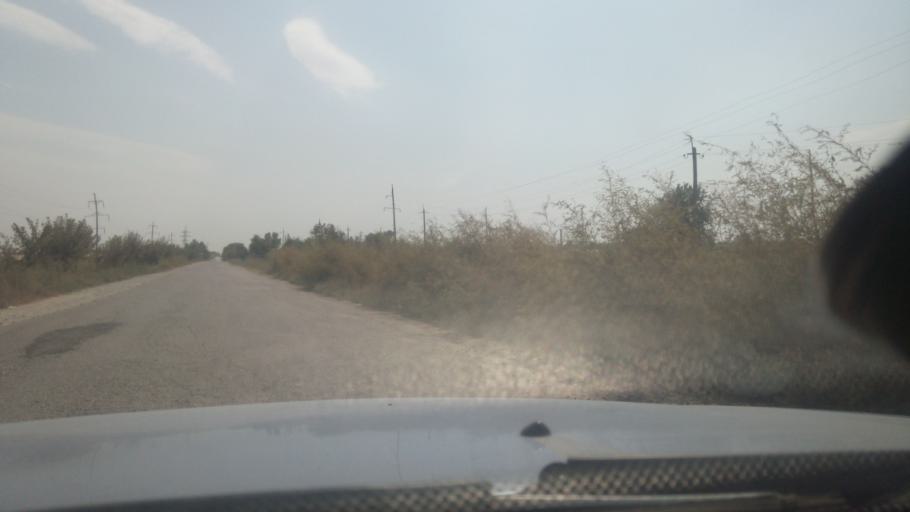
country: UZ
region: Sirdaryo
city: Guliston
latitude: 40.5323
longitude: 68.7663
